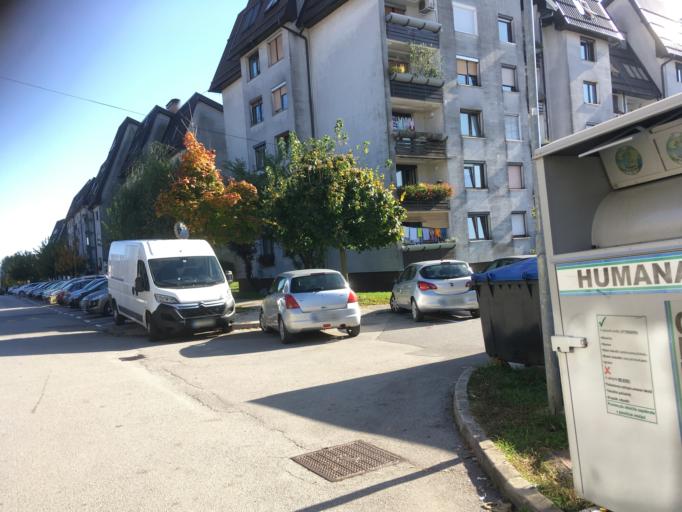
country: SI
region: Menges
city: Menges
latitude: 46.1674
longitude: 14.5746
